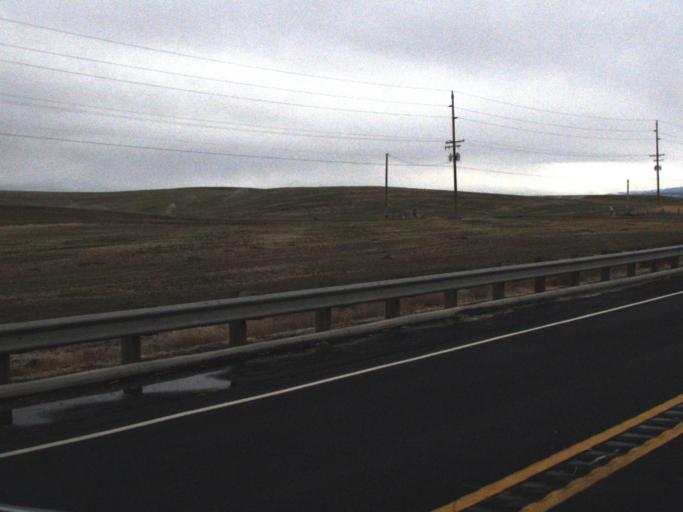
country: US
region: Washington
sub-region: Walla Walla County
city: Garrett
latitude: 46.0498
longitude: -118.5253
